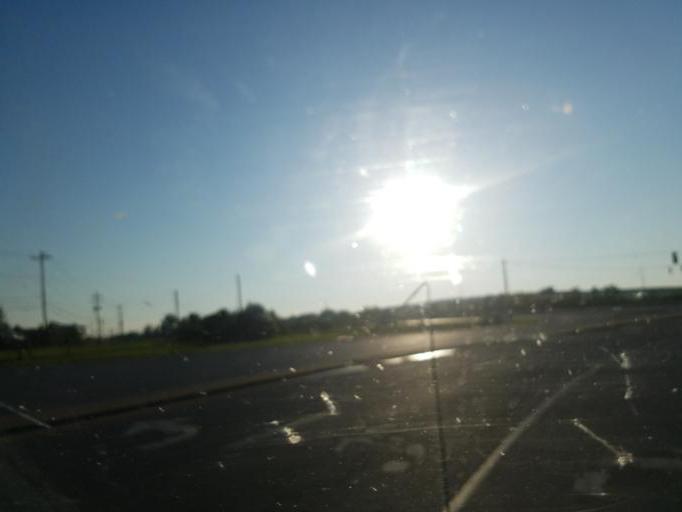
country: US
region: Kentucky
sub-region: Jefferson County
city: Heritage Creek
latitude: 38.1359
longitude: -85.7128
